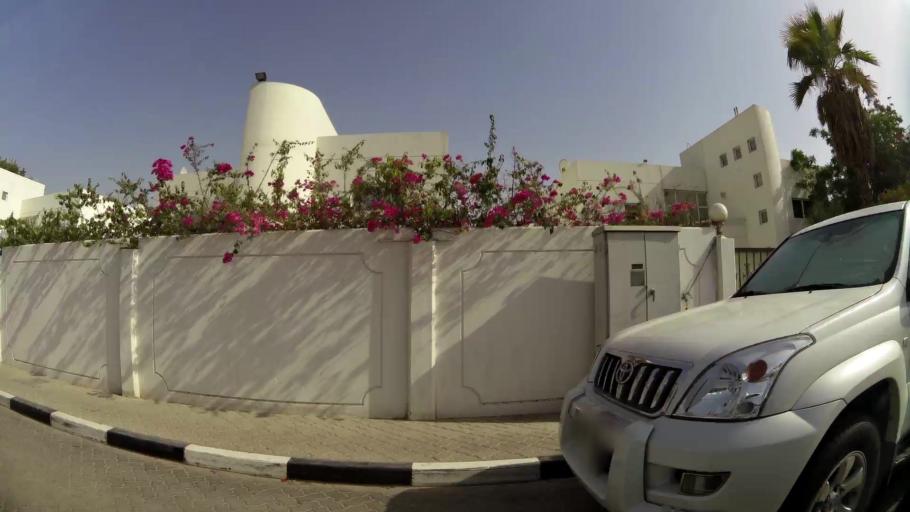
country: AE
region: Ash Shariqah
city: Sharjah
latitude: 25.2462
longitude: 55.3459
